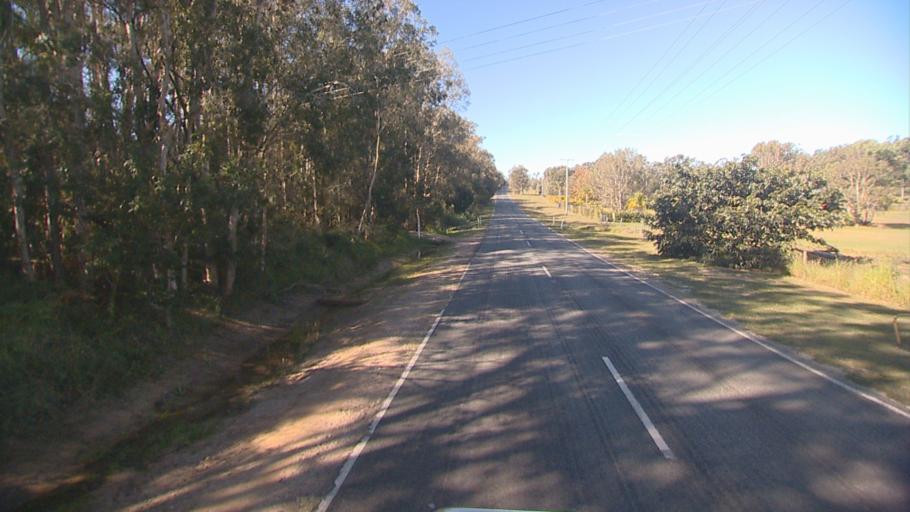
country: AU
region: Queensland
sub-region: Logan
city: Logan Reserve
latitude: -27.7193
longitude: 153.0695
